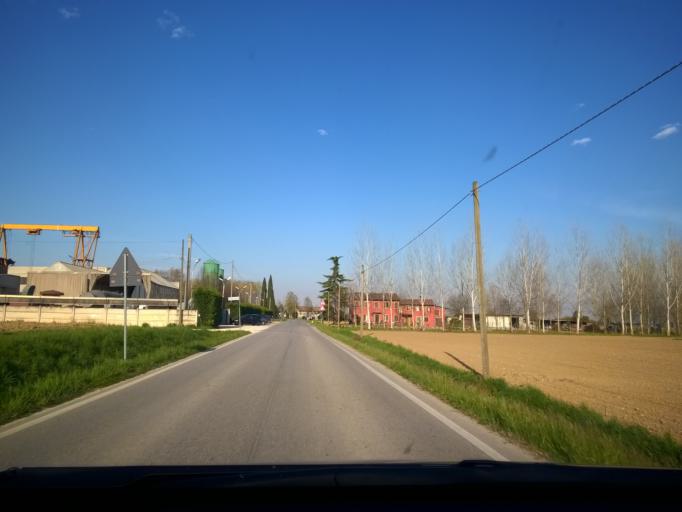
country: IT
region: Veneto
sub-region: Provincia di Treviso
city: San Biagio di Callalta
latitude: 45.7076
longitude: 12.3767
